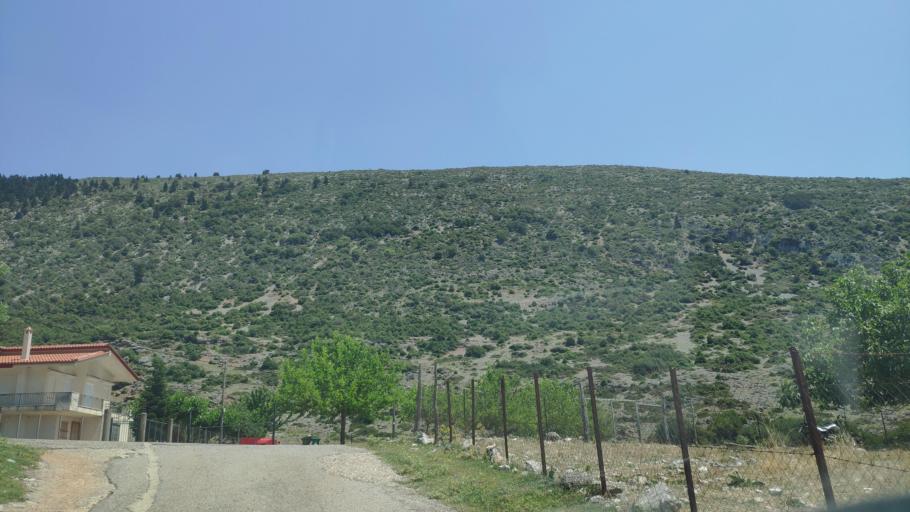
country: GR
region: West Greece
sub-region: Nomos Aitolias kai Akarnanias
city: Krikellos
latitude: 39.0532
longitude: 21.3671
